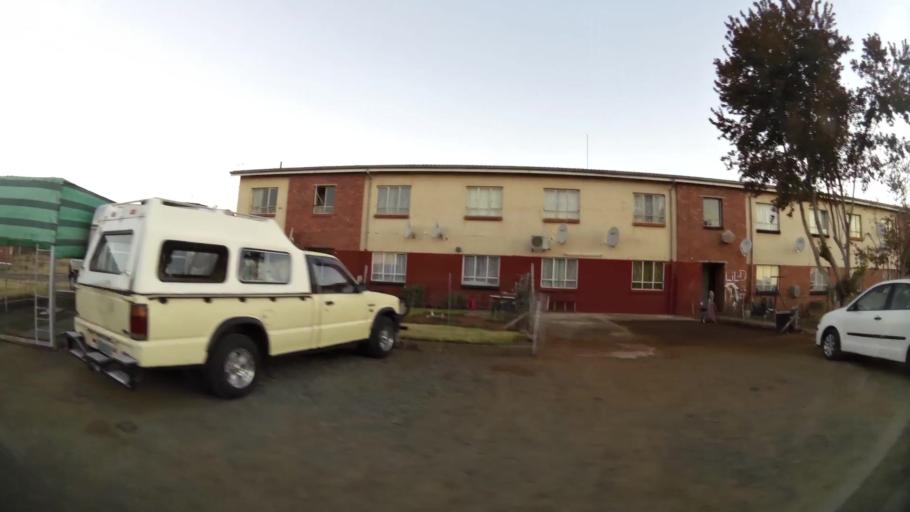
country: ZA
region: Northern Cape
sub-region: Frances Baard District Municipality
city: Kimberley
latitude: -28.7209
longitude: 24.7779
